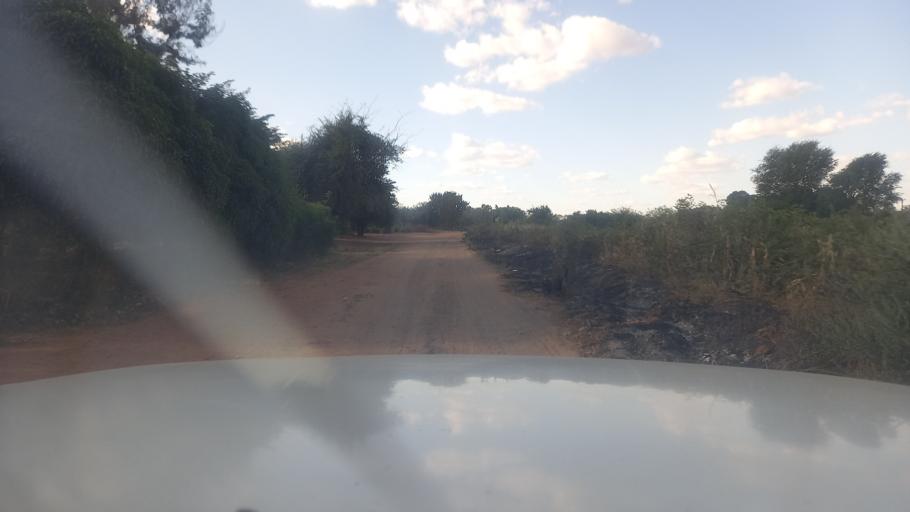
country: ZM
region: Southern
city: Livingstone
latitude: -17.8299
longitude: 25.8678
